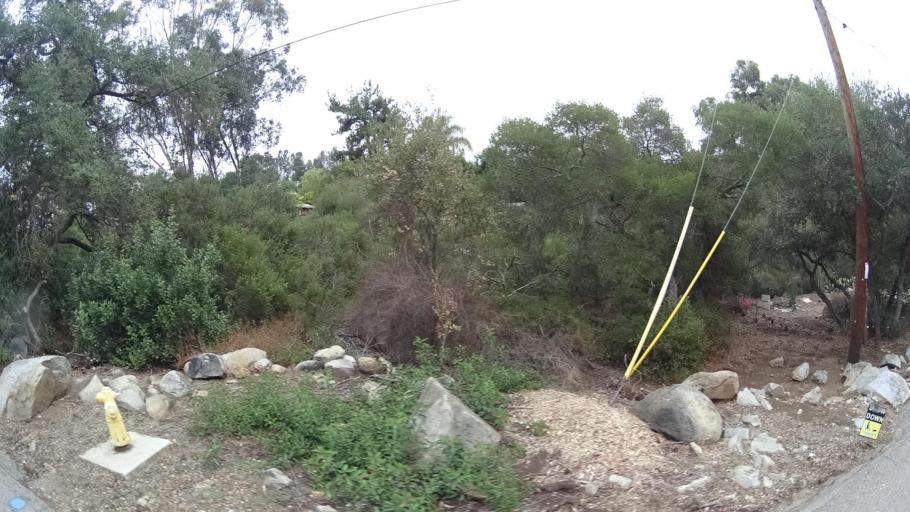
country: US
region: California
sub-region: San Diego County
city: Escondido
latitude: 33.0799
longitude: -117.1190
